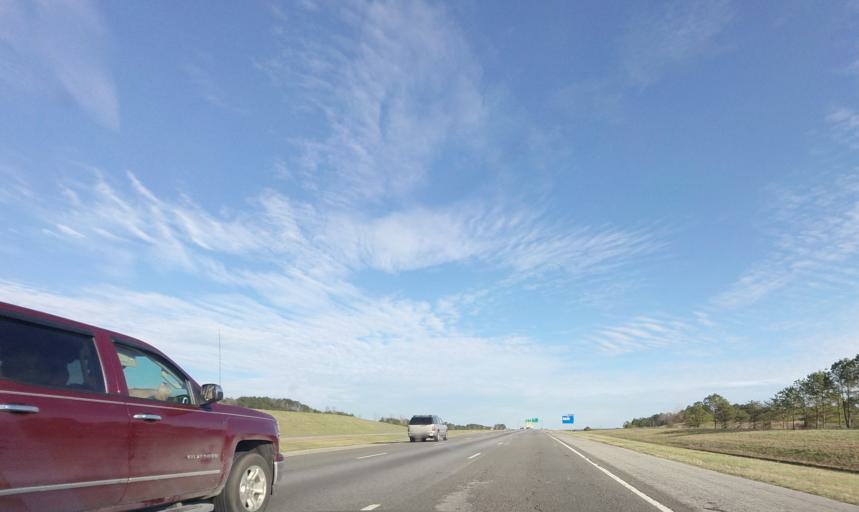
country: US
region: Alabama
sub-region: Walker County
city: Jasper
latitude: 33.8569
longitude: -87.3611
